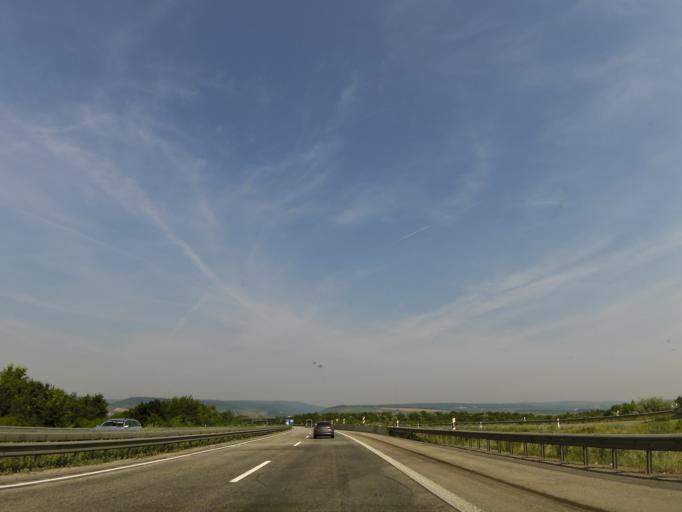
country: DE
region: Rheinland-Pfalz
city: Gensingen
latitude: 49.9260
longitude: 7.9424
